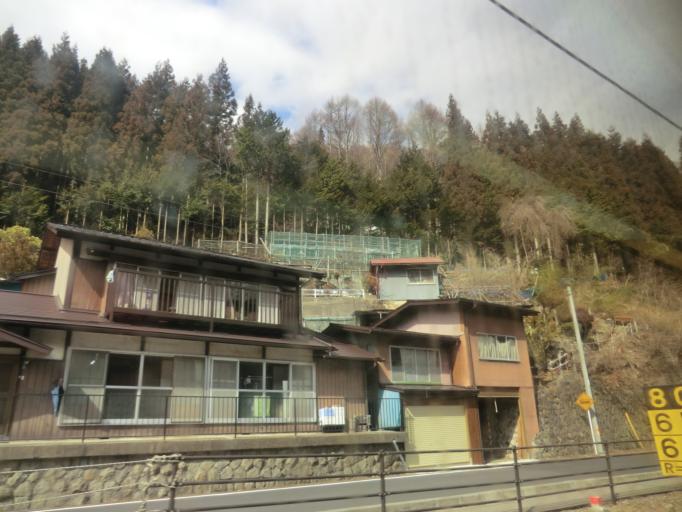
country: JP
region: Nagano
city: Tatsuno
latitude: 35.9718
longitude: 137.8180
